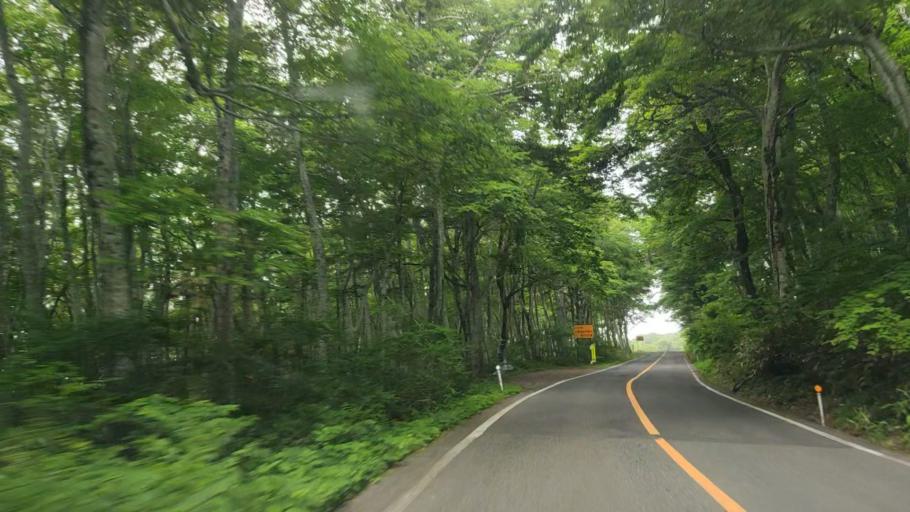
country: JP
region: Tottori
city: Yonago
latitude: 35.3542
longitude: 133.5396
